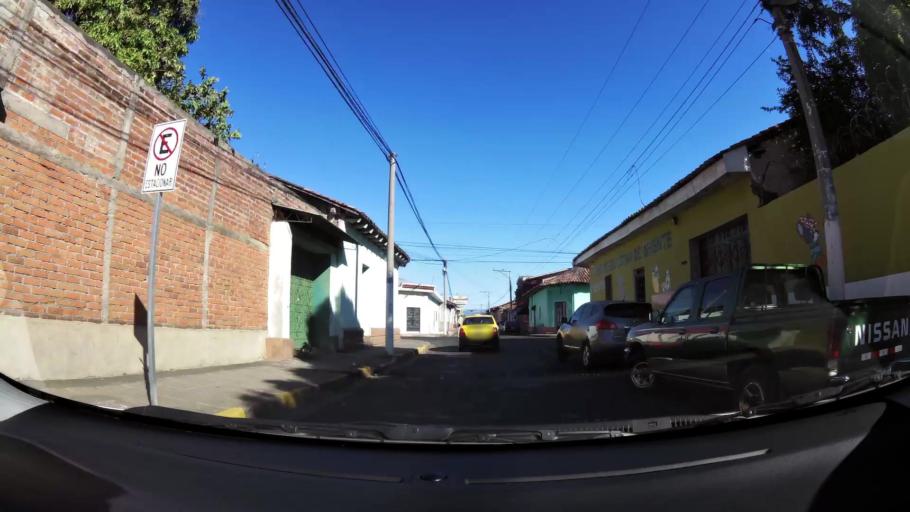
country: SV
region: San Miguel
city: San Miguel
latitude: 13.4757
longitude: -88.1776
